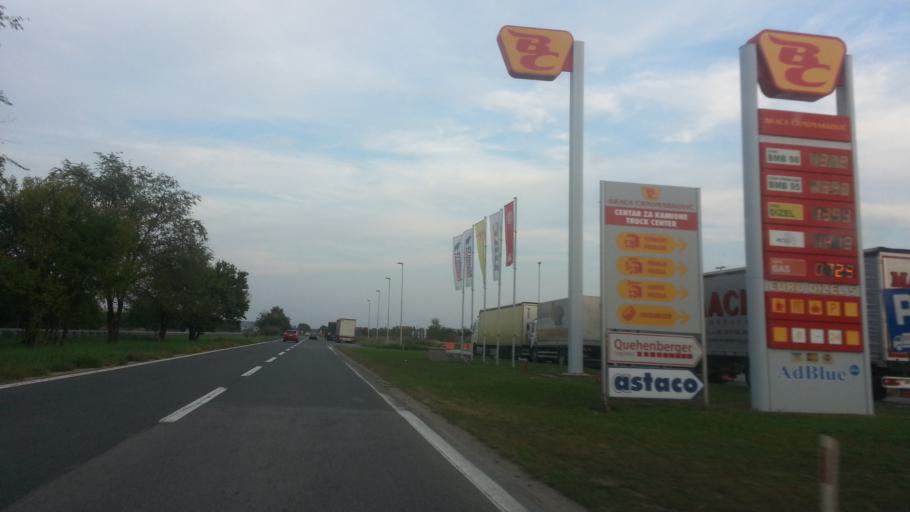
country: RS
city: Novi Banovci
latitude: 44.8849
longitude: 20.3084
